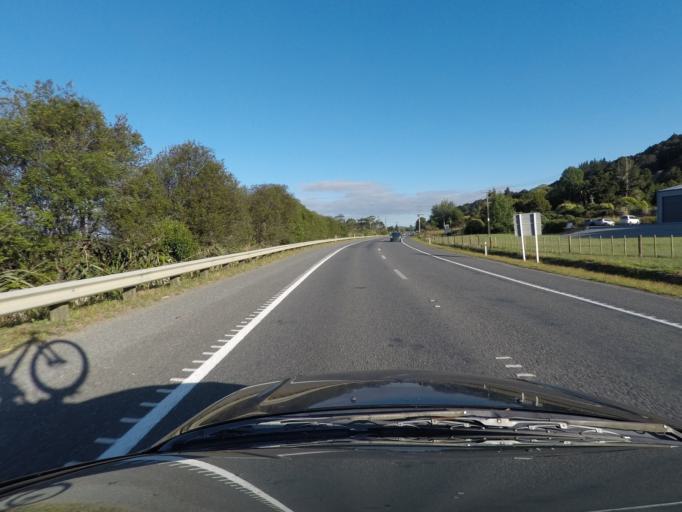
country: NZ
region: Northland
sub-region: Whangarei
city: Whangarei
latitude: -35.6232
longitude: 174.2911
